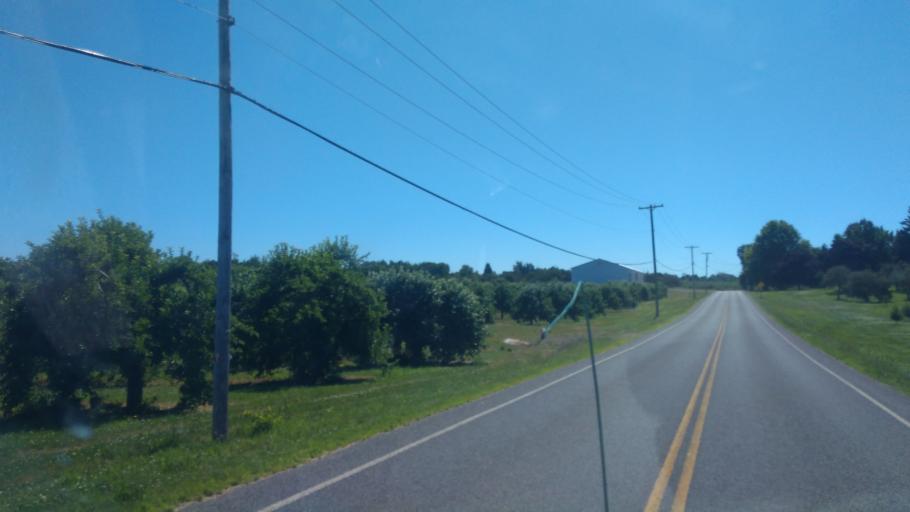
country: US
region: New York
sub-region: Wayne County
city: Sodus
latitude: 43.2745
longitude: -77.1107
